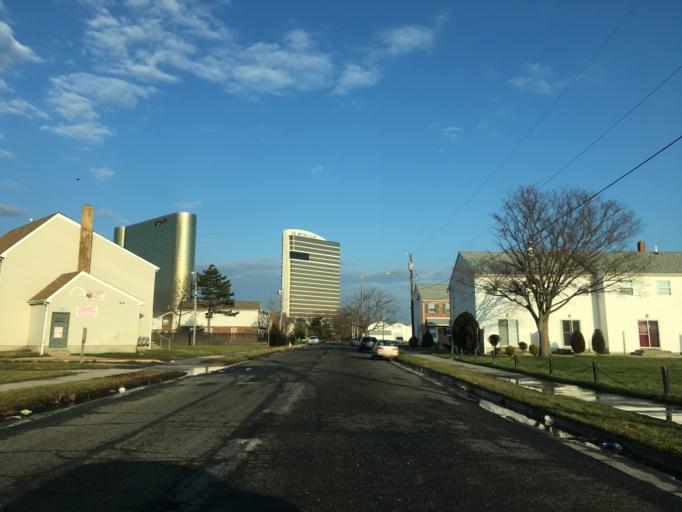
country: US
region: New Jersey
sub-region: Atlantic County
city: Atlantic City
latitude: 39.3730
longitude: -74.4290
